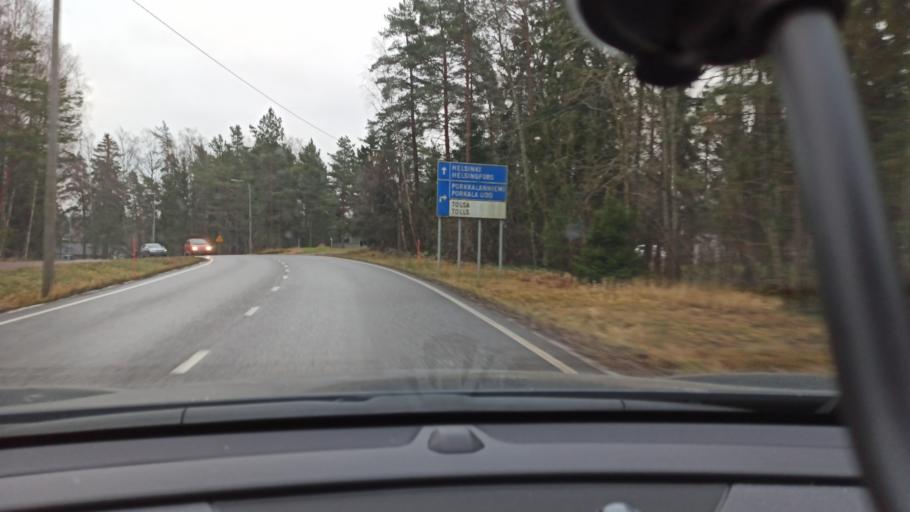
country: FI
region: Uusimaa
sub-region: Helsinki
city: Kirkkonummi
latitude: 60.1263
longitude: 24.4670
